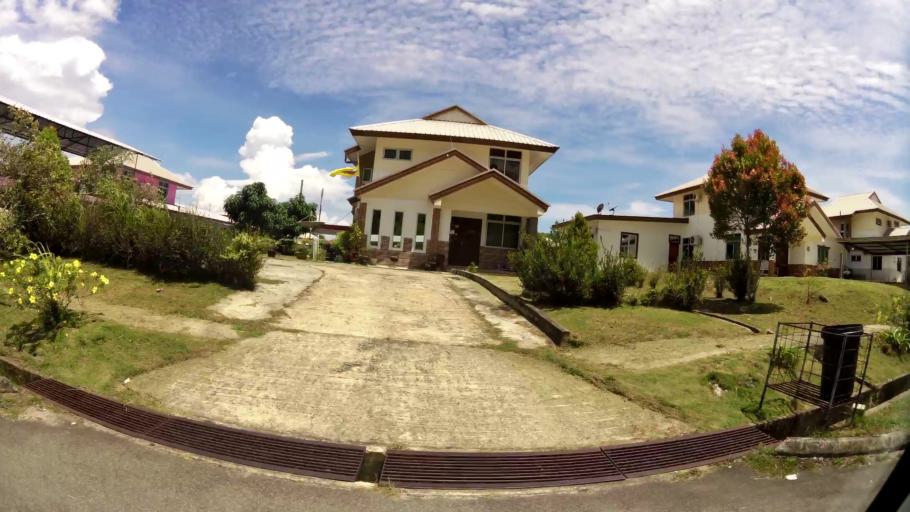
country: BN
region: Brunei and Muara
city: Bandar Seri Begawan
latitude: 4.9682
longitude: 114.9046
